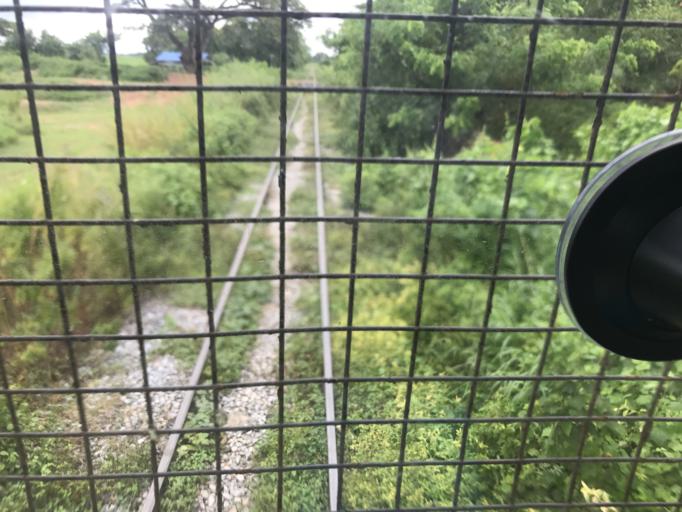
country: MM
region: Bago
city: Paungde
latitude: 18.6718
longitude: 95.4061
